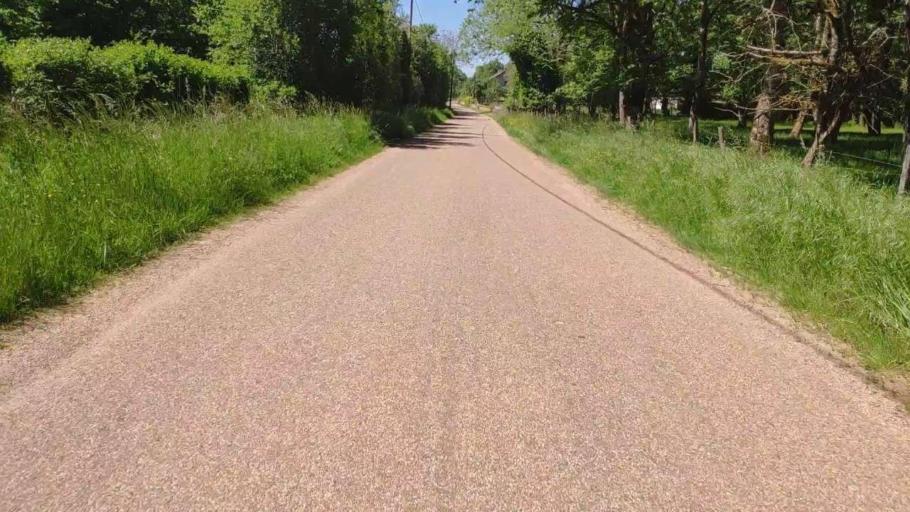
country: FR
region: Franche-Comte
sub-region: Departement du Jura
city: Poligny
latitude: 46.7291
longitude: 5.7514
